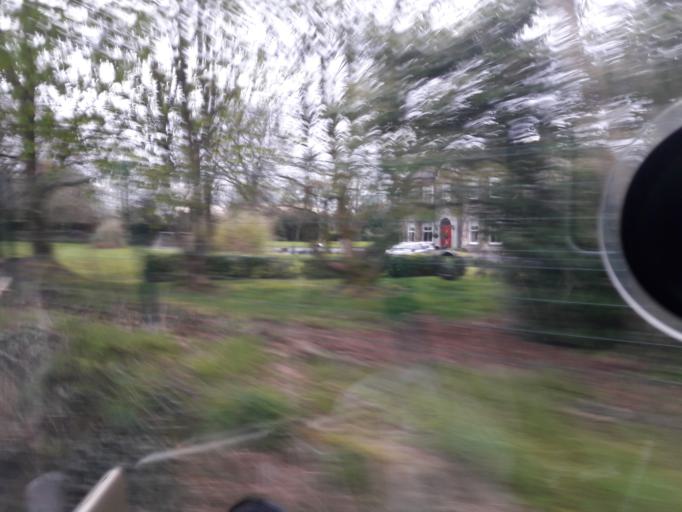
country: IE
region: Leinster
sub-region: An Iarmhi
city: An Muileann gCearr
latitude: 53.6183
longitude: -7.4126
